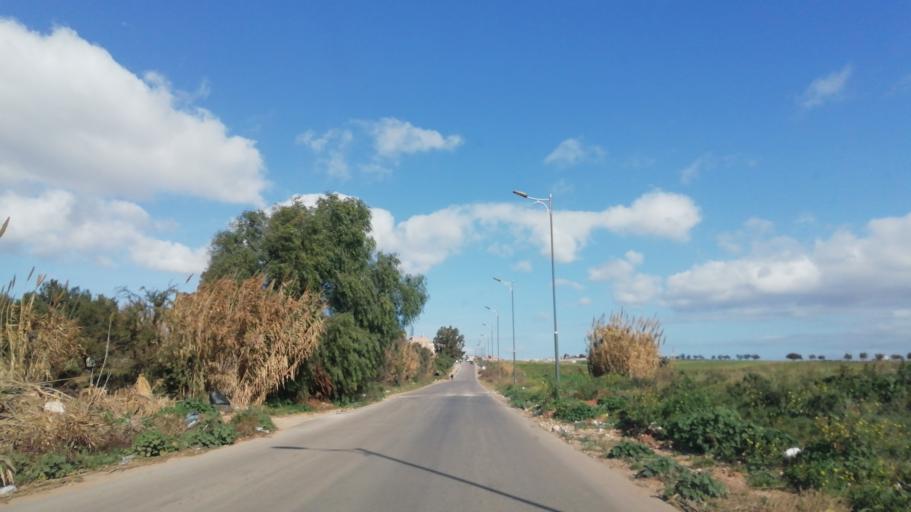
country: DZ
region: Oran
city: Es Senia
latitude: 35.6275
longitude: -0.6616
